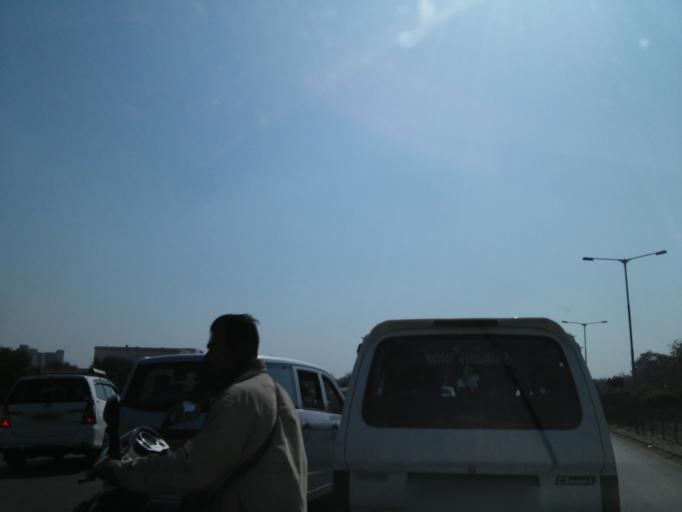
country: IN
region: Gujarat
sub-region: Ahmadabad
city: Ahmedabad
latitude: 23.0824
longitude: 72.5270
